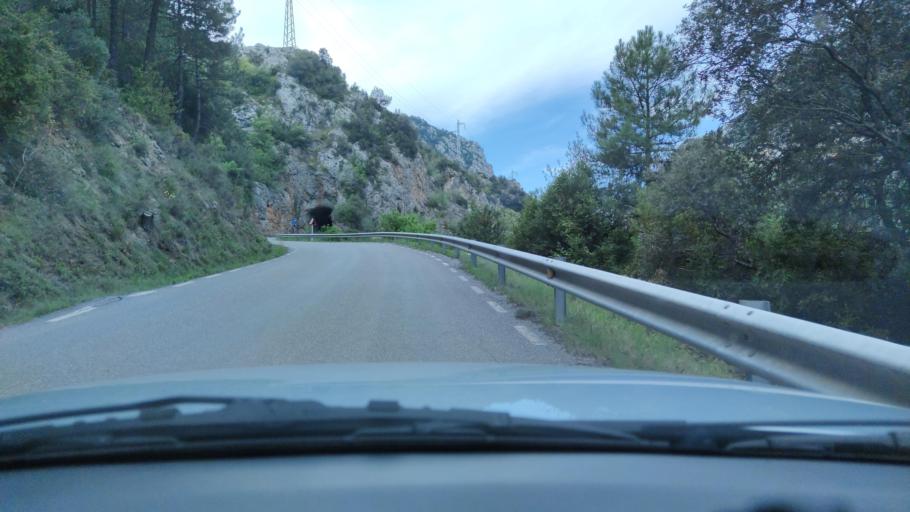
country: ES
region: Catalonia
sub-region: Provincia de Lleida
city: Coll de Nargo
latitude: 42.2491
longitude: 1.3490
